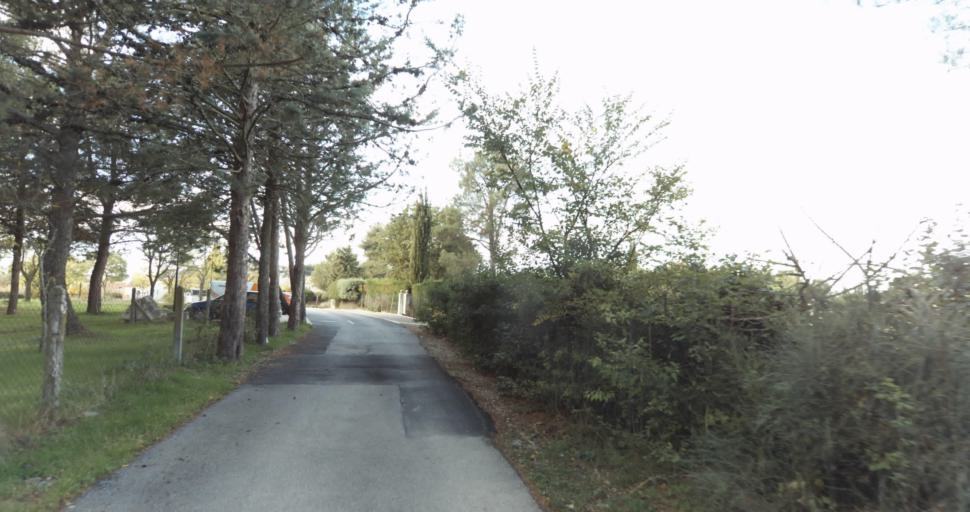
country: FR
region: Provence-Alpes-Cote d'Azur
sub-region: Departement des Bouches-du-Rhone
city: Venelles
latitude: 43.5996
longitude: 5.4915
